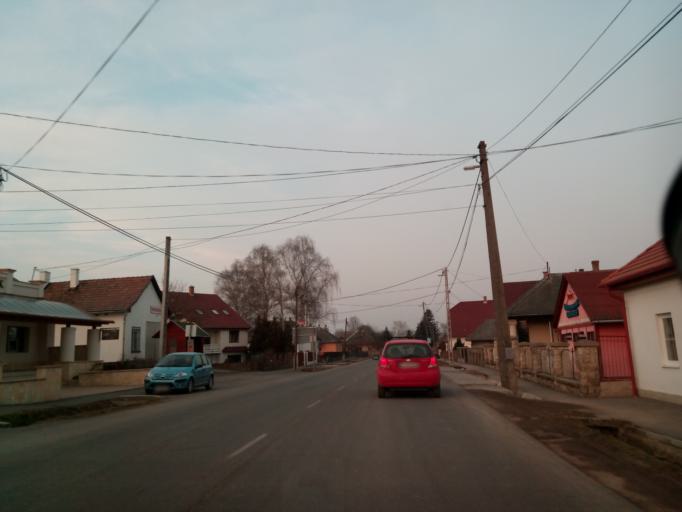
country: HU
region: Borsod-Abauj-Zemplen
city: Gonc
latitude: 48.5005
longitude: 21.2306
